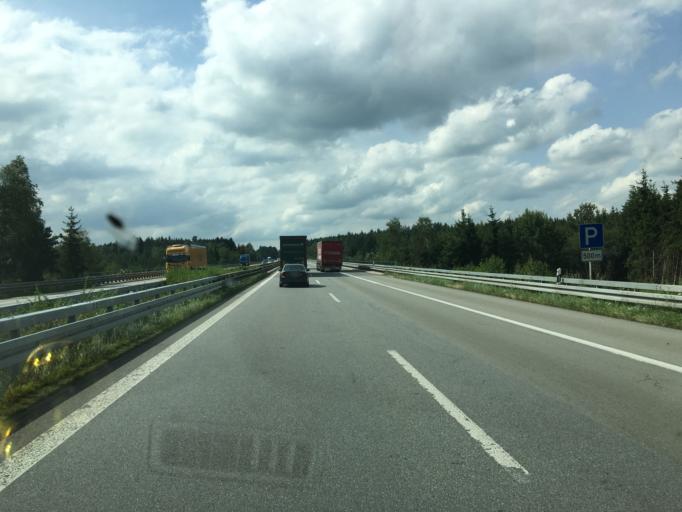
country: DE
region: Bavaria
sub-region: Lower Bavaria
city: Tiefenbach
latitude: 48.6145
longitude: 13.3584
